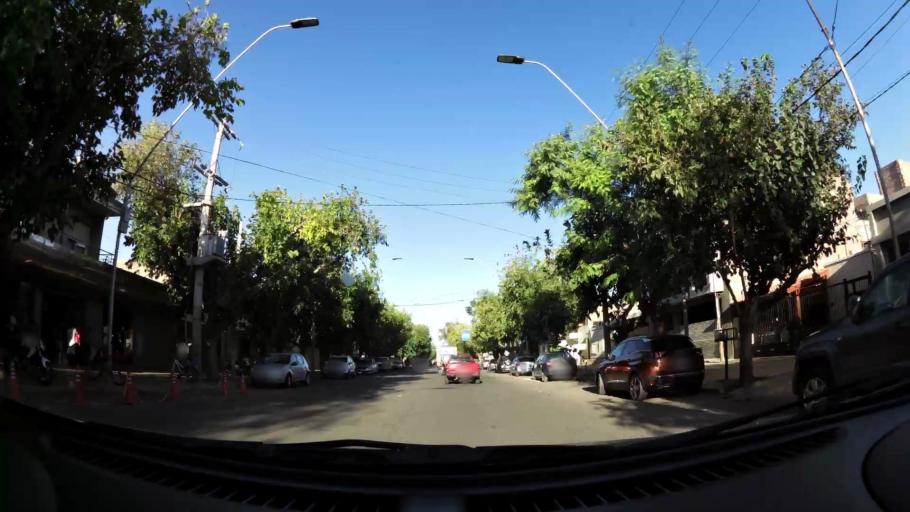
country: AR
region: San Juan
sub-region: Departamento de Santa Lucia
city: Santa Lucia
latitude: -31.5335
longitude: -68.5127
